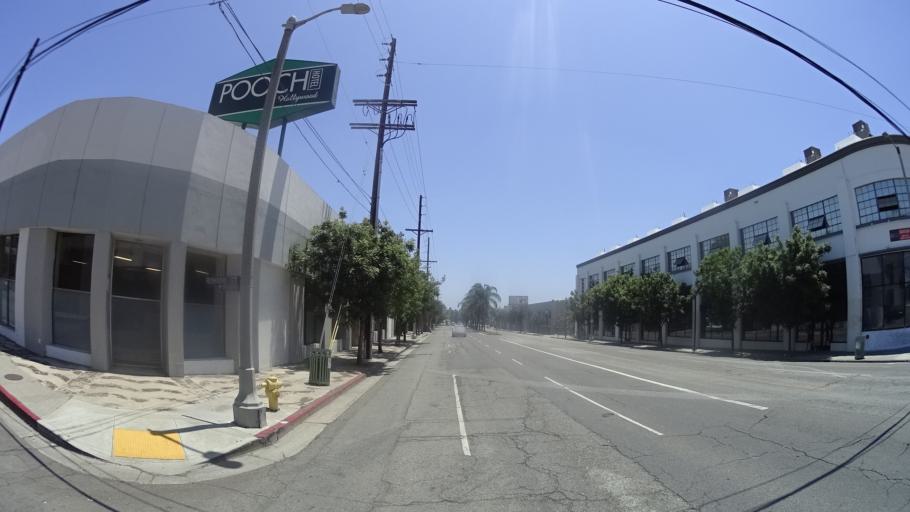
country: US
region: California
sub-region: Los Angeles County
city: Hollywood
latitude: 34.0889
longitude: -118.3386
